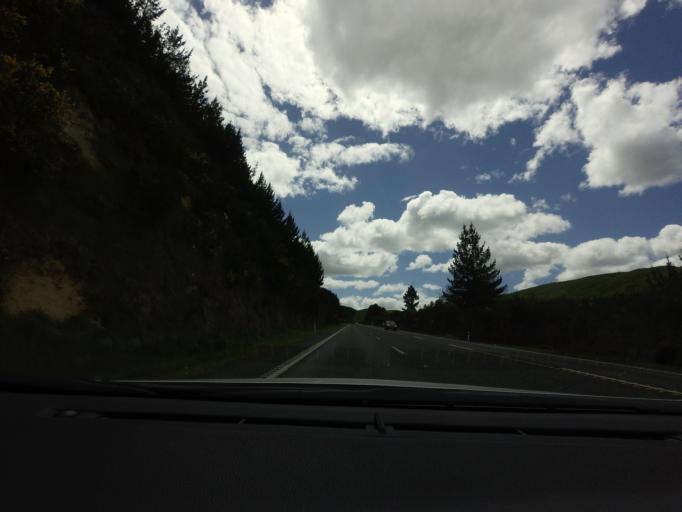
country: NZ
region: Bay of Plenty
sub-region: Rotorua District
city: Rotorua
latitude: -38.2920
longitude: 176.3539
